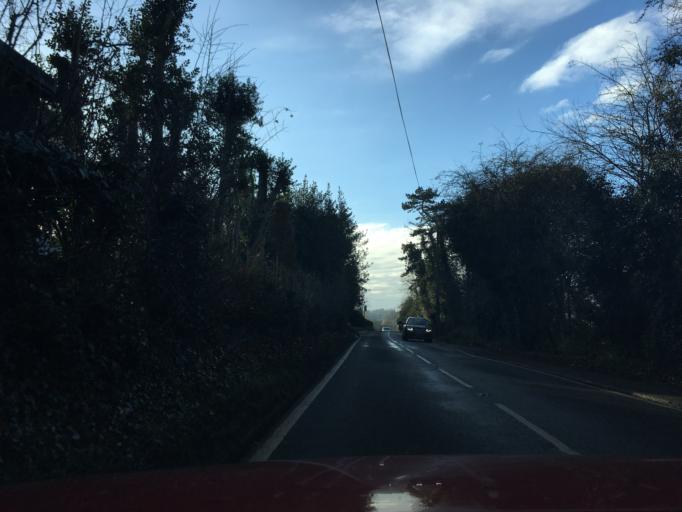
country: GB
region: England
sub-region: Staffordshire
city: Burton upon Trent
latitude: 52.8191
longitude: -1.6071
